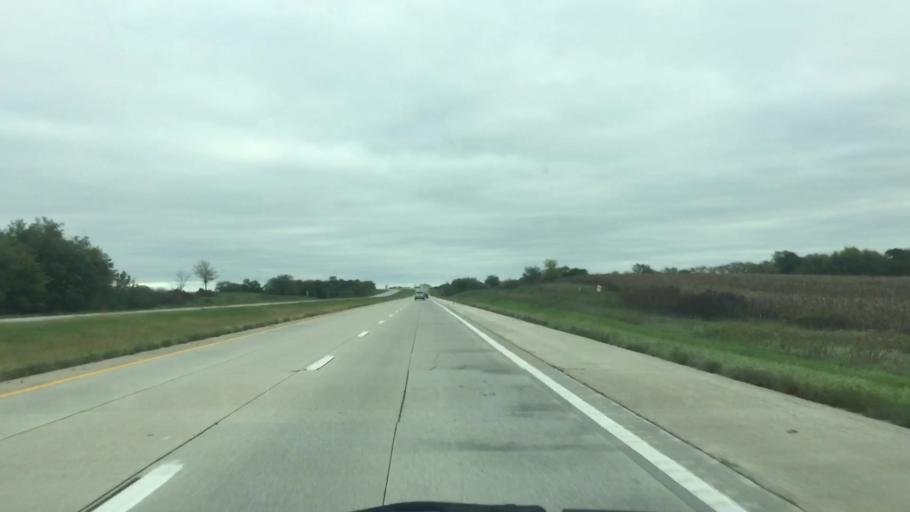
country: US
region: Missouri
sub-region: Daviess County
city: Gallatin
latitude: 39.9646
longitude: -94.1004
